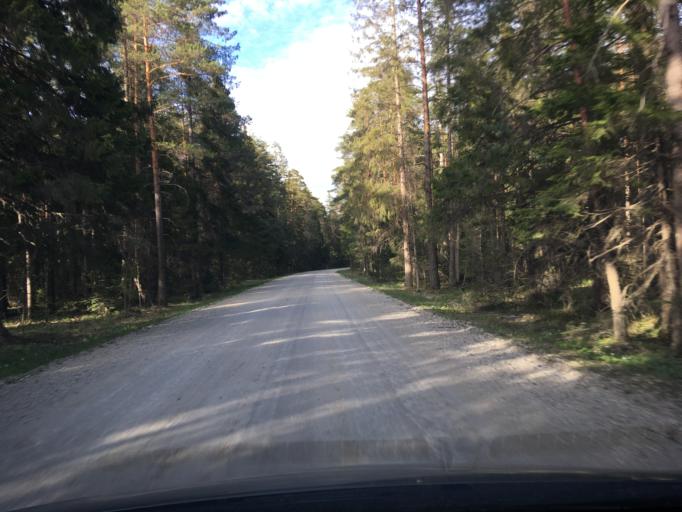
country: EE
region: Raplamaa
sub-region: Maerjamaa vald
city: Marjamaa
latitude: 59.0221
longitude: 24.4370
